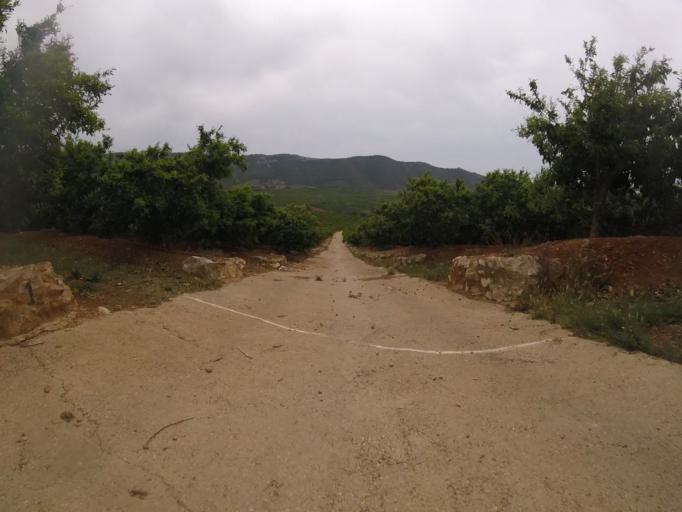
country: ES
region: Valencia
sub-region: Provincia de Castello
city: Alcala de Xivert
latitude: 40.2794
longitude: 0.2505
